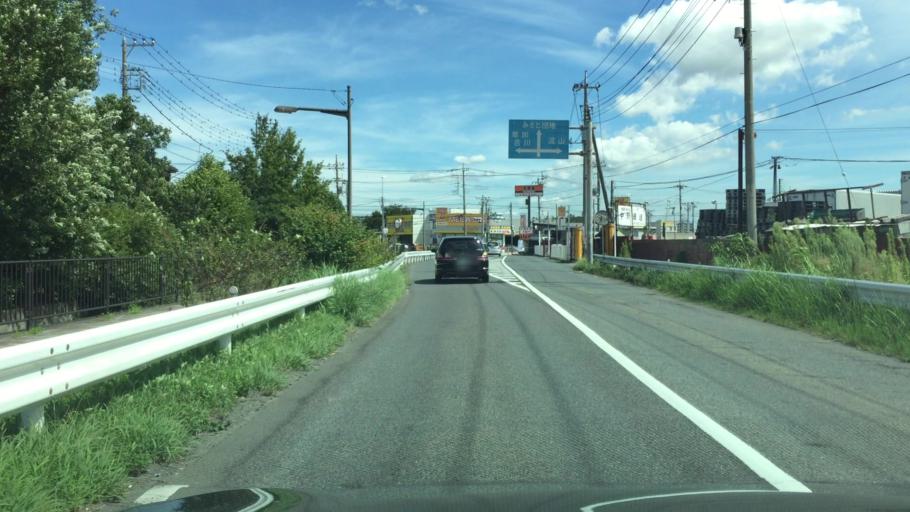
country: JP
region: Saitama
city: Yashio-shi
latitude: 35.8485
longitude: 139.8534
